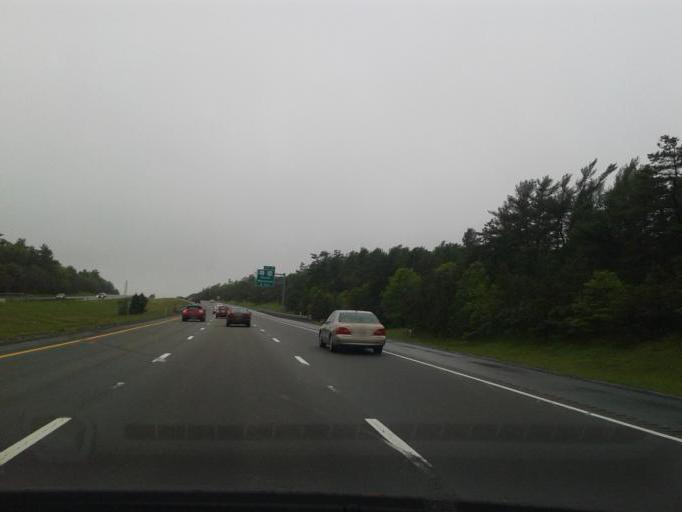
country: US
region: Massachusetts
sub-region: Plymouth County
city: White Island Shores
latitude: 41.7746
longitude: -70.6374
